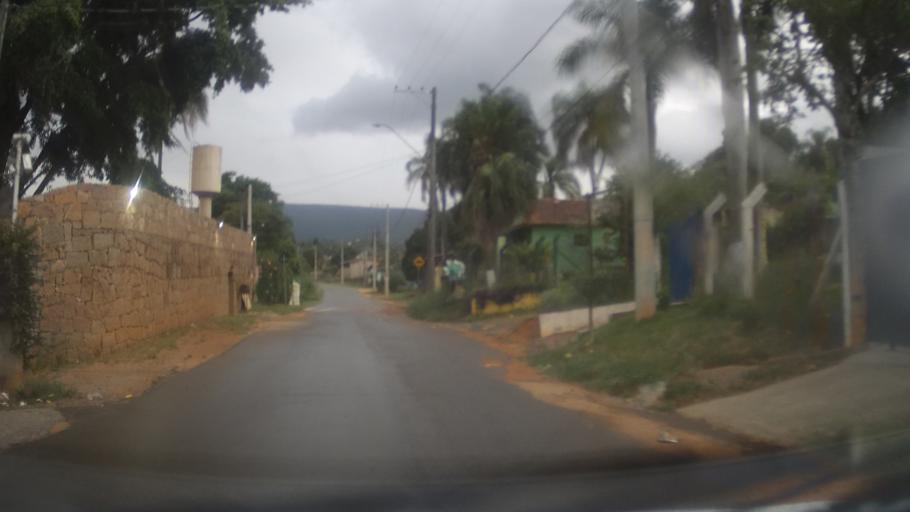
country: BR
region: Sao Paulo
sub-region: Itupeva
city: Itupeva
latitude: -23.1867
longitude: -47.0155
